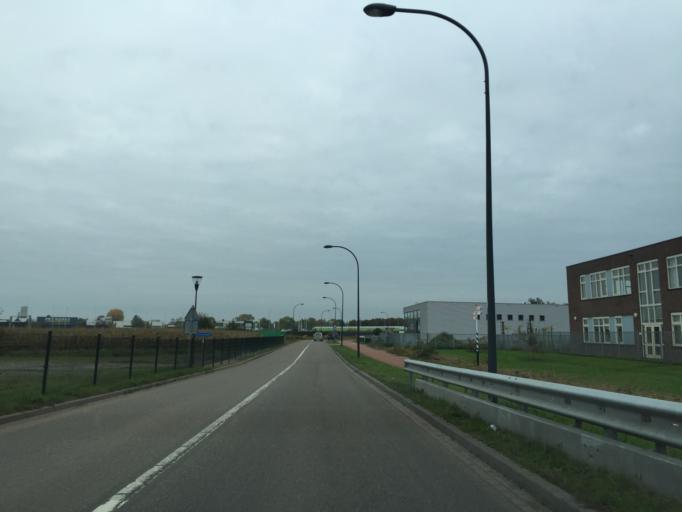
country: NL
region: North Brabant
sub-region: Gemeente Waalwijk
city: Waalwijk
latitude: 51.6743
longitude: 5.0490
